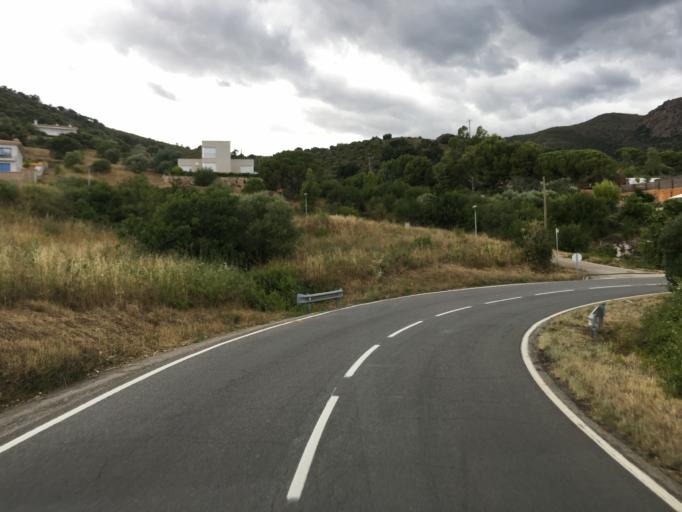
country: ES
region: Catalonia
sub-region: Provincia de Girona
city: Llanca
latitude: 42.3387
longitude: 3.1896
